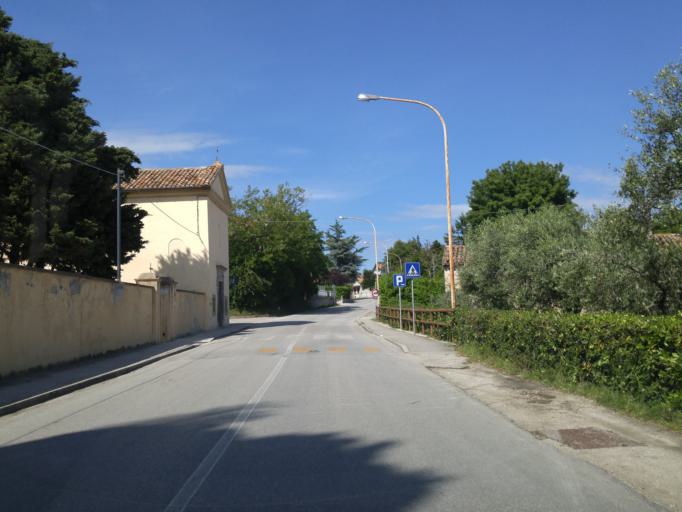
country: IT
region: The Marches
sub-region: Provincia di Pesaro e Urbino
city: San Costanzo
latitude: 43.7599
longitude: 13.0661
